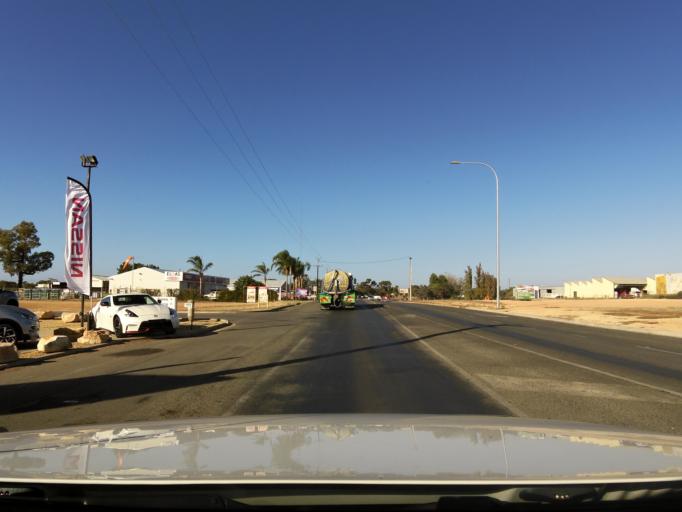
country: AU
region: South Australia
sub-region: Berri and Barmera
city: Berri
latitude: -34.2611
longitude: 140.6143
